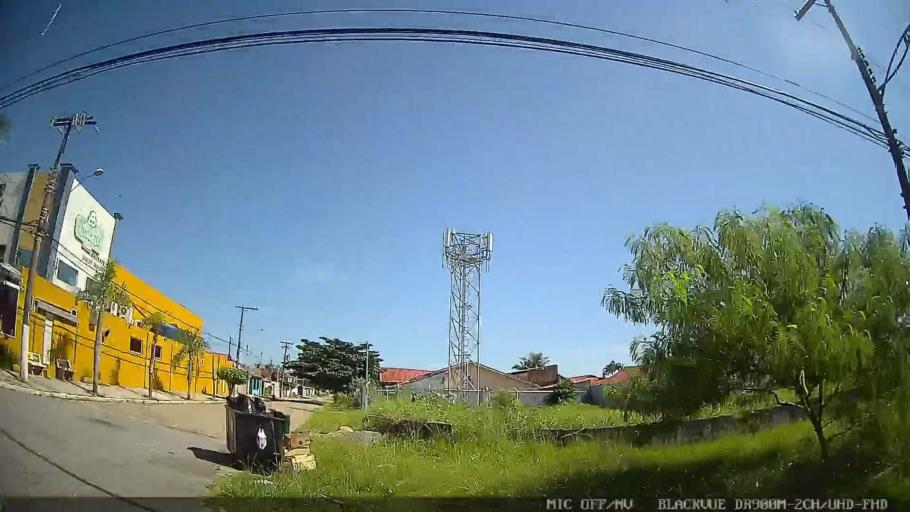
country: BR
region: Sao Paulo
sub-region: Peruibe
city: Peruibe
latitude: -24.2959
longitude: -46.9684
